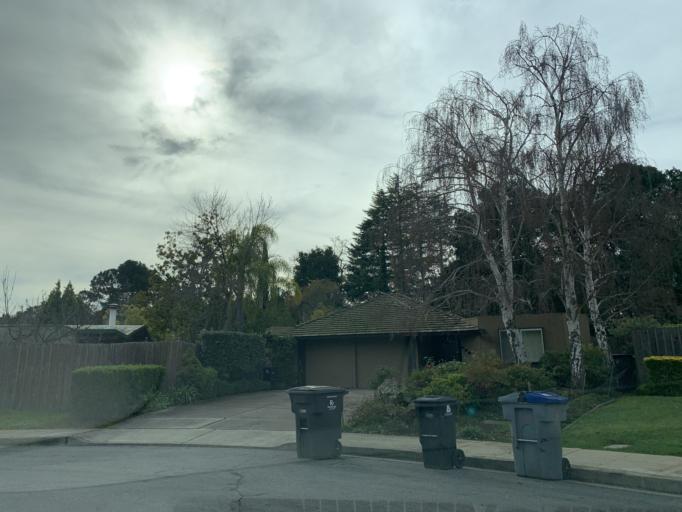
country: US
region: California
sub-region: Santa Clara County
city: Mountain View
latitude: 37.3829
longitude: -122.0896
